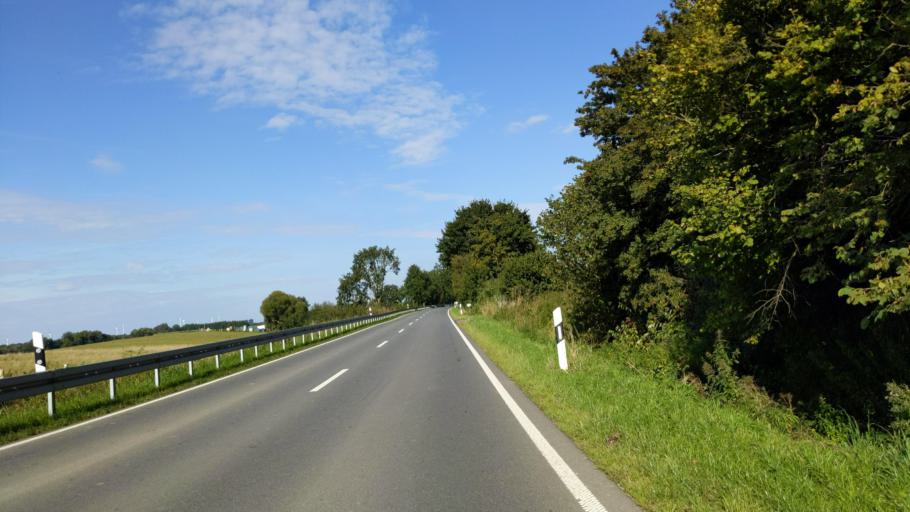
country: DE
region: Schleswig-Holstein
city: Stockelsdorf
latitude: 53.9586
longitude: 10.6335
